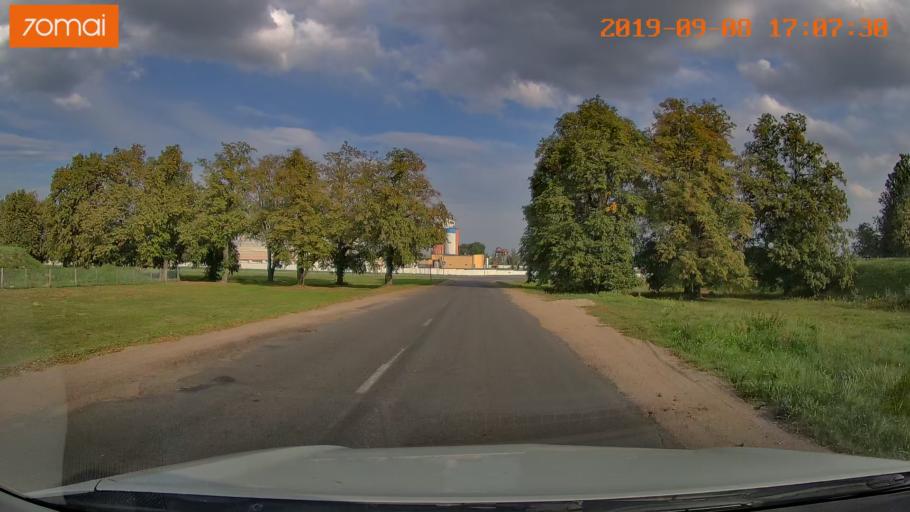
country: BY
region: Grodnenskaya
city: Hrodna
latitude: 53.6650
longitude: 23.9632
